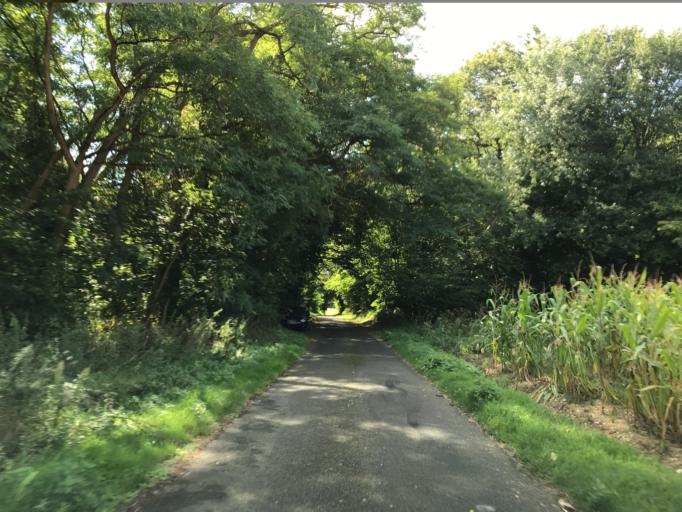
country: FR
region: Haute-Normandie
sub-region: Departement de l'Eure
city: Saint-Just
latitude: 49.1485
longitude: 1.4058
